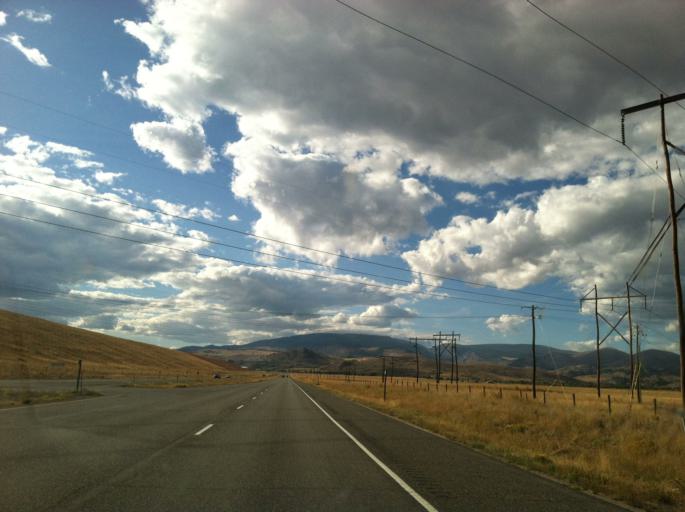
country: US
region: Montana
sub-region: Deer Lodge County
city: Anaconda
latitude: 46.1189
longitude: -112.8750
